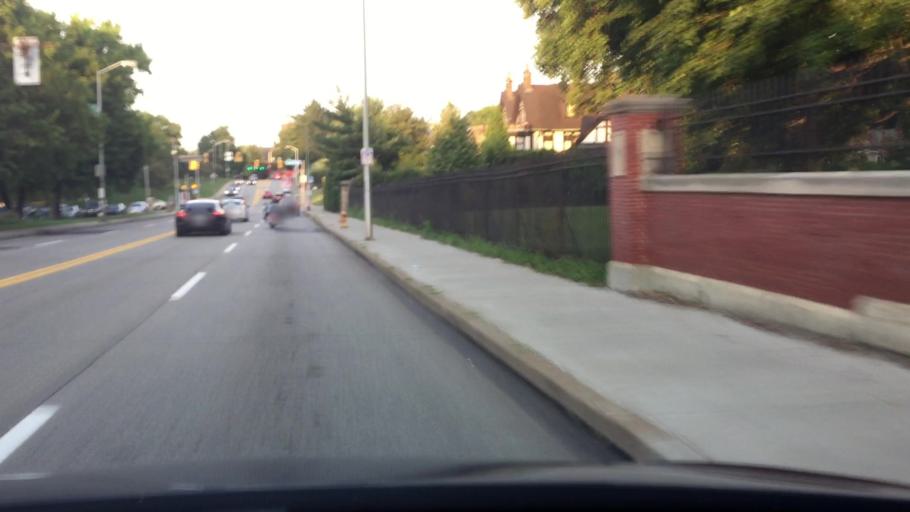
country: US
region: Pennsylvania
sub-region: Allegheny County
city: Bloomfield
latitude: 40.4534
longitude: -79.9167
